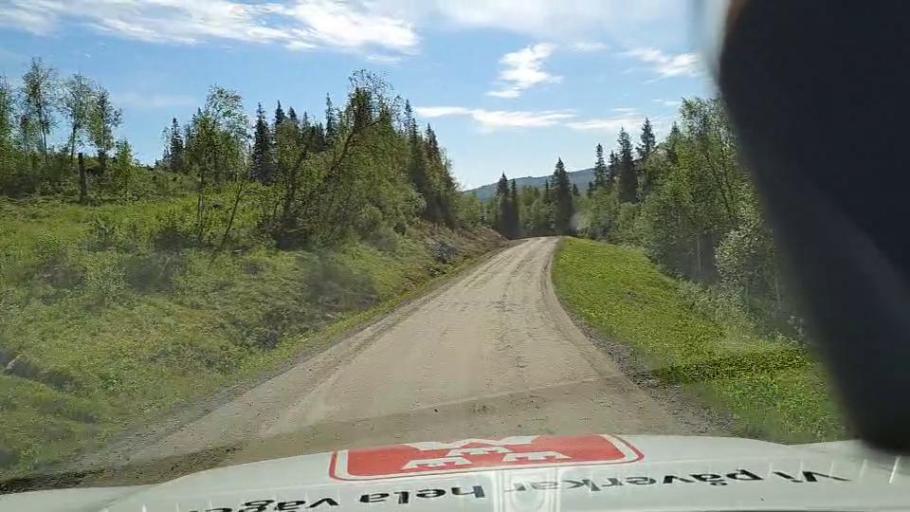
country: NO
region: Nord-Trondelag
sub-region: Lierne
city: Sandvika
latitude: 64.6083
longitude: 13.7084
